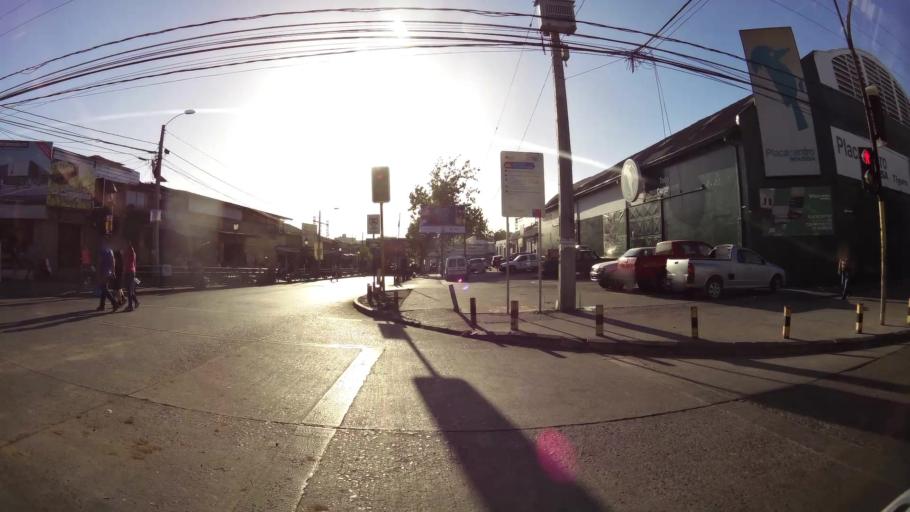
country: CL
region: Maule
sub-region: Provincia de Talca
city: Talca
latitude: -35.4285
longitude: -71.6480
